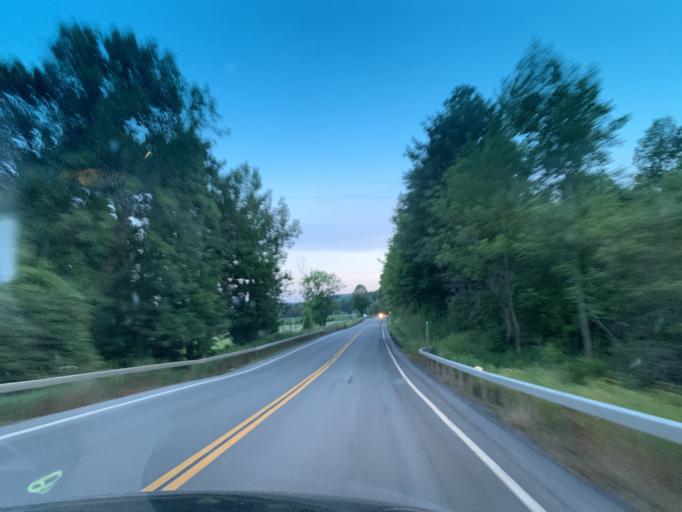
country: US
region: New York
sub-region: Chenango County
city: New Berlin
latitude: 42.6981
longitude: -75.3225
